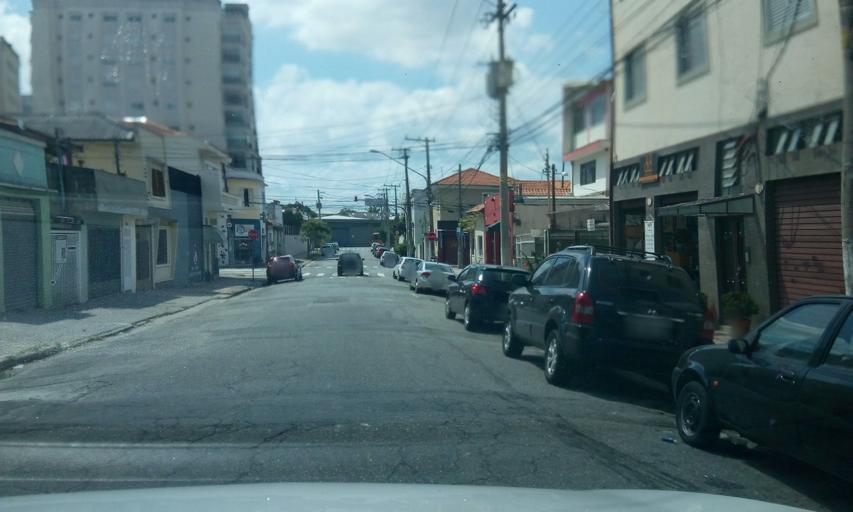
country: BR
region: Sao Paulo
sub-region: Sao Paulo
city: Sao Paulo
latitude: -23.5219
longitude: -46.7105
